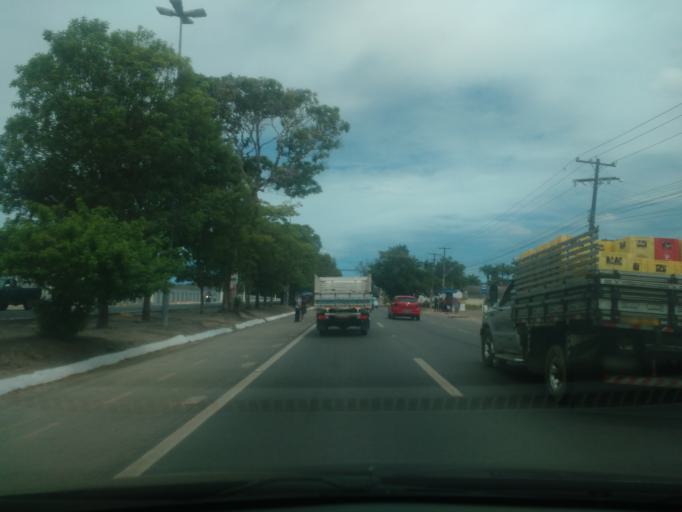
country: BR
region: Alagoas
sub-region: Satuba
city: Satuba
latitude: -9.5492
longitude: -35.7864
